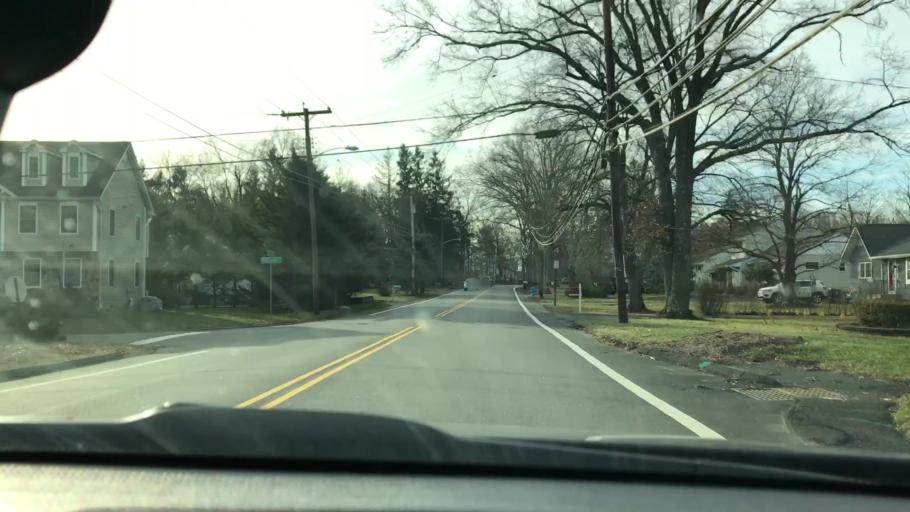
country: US
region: New Jersey
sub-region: Morris County
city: Parsippany
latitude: 40.8379
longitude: -74.4213
